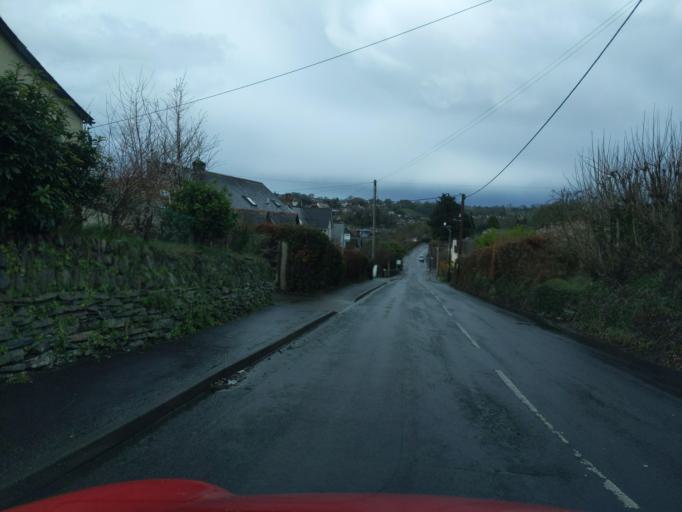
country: GB
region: England
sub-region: Devon
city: Tavistock
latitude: 50.5438
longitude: -4.1440
